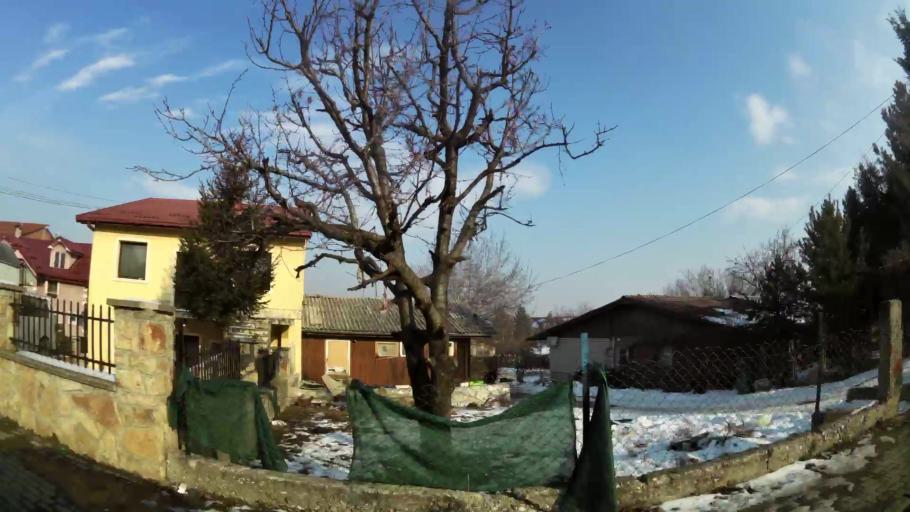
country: MK
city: Creshevo
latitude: 42.0150
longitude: 21.5054
